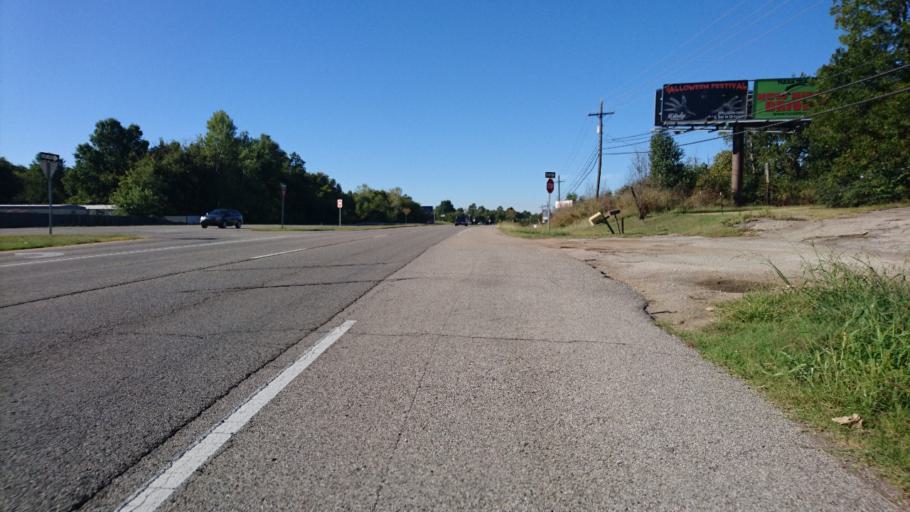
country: US
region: Oklahoma
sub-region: Rogers County
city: Catoosa
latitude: 36.1956
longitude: -95.7309
